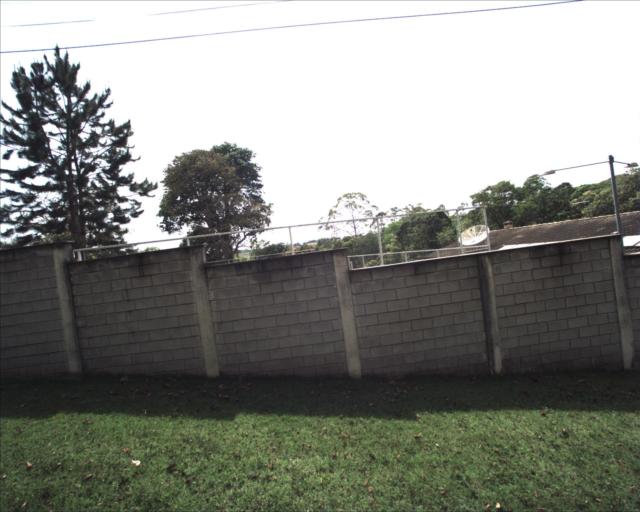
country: BR
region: Sao Paulo
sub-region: Salto De Pirapora
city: Salto de Pirapora
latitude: -23.5615
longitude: -47.5364
